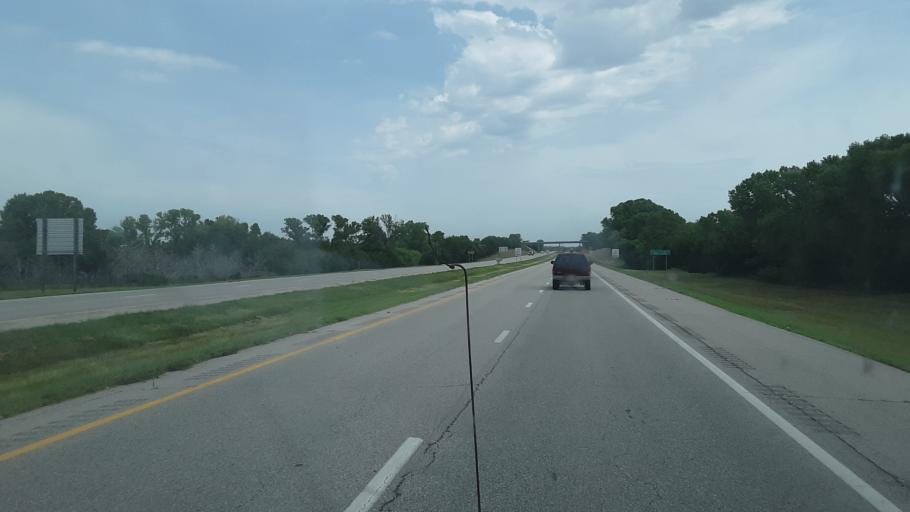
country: US
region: Kansas
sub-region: Sedgwick County
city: Kechi
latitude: 37.7752
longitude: -97.2918
